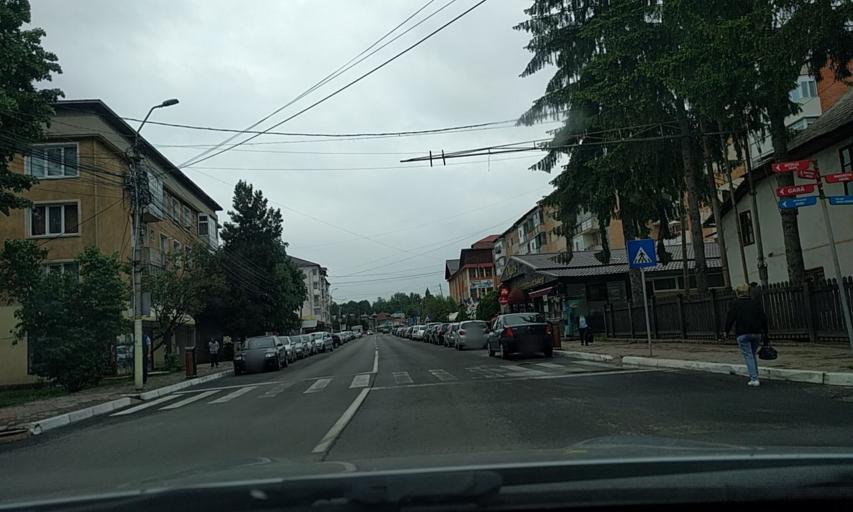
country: RO
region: Dambovita
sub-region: Oras Pucioasa
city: Pucioasa
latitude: 45.0760
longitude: 25.4345
